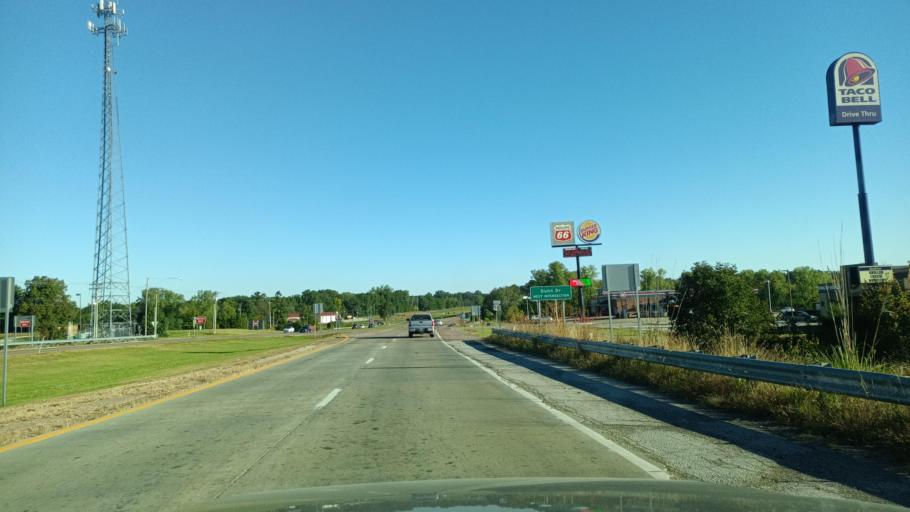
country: US
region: Missouri
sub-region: Callaway County
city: Fulton
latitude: 38.9452
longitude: -91.9409
